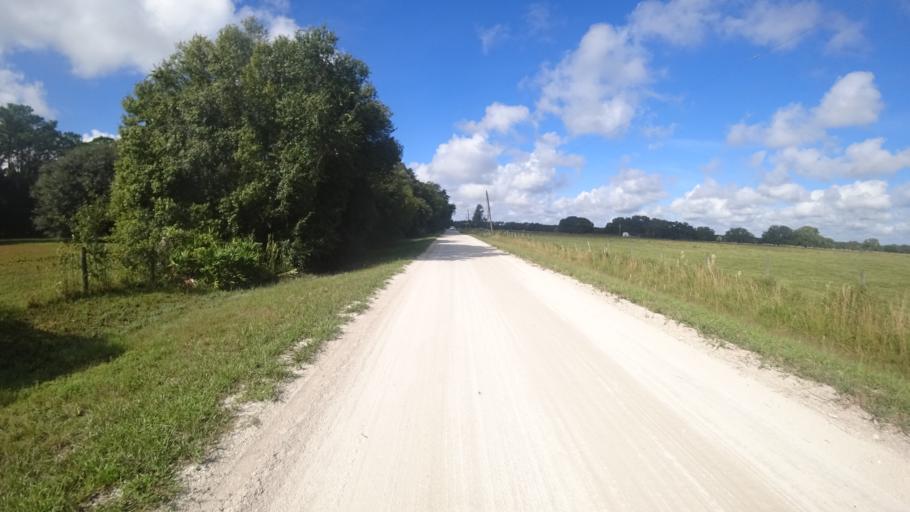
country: US
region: Florida
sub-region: Sarasota County
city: Lake Sarasota
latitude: 27.3068
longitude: -82.2214
